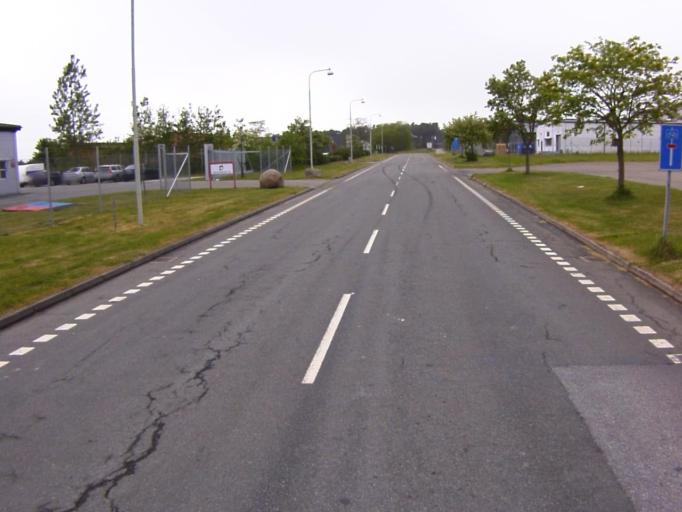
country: SE
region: Skane
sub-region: Kristianstads Kommun
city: Ahus
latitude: 55.9310
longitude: 14.2818
